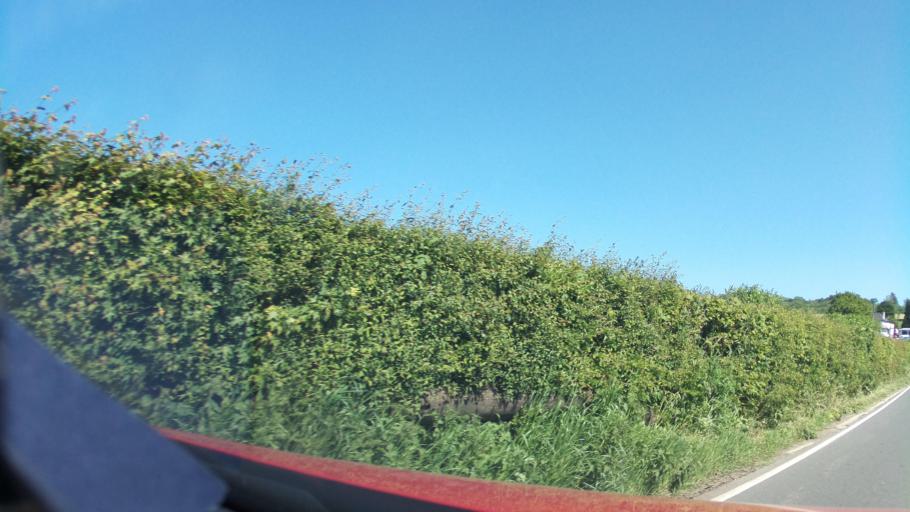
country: GB
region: England
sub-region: Somerset
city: Chard
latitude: 50.8674
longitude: -3.0575
